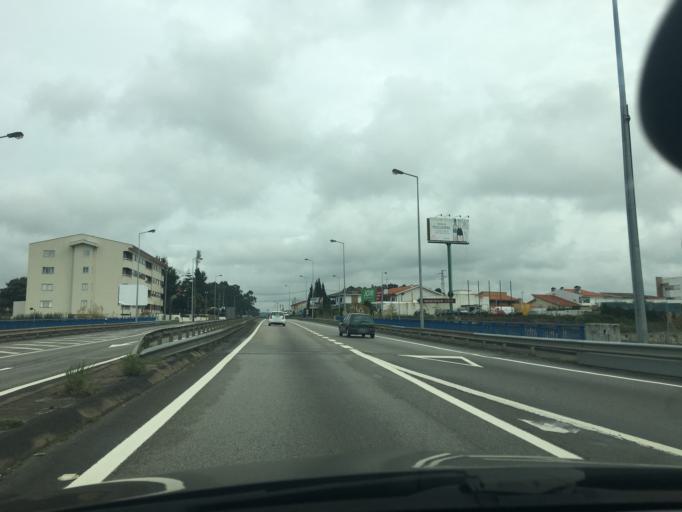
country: PT
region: Porto
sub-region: Maia
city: Maia
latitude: 41.2407
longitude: -8.6238
